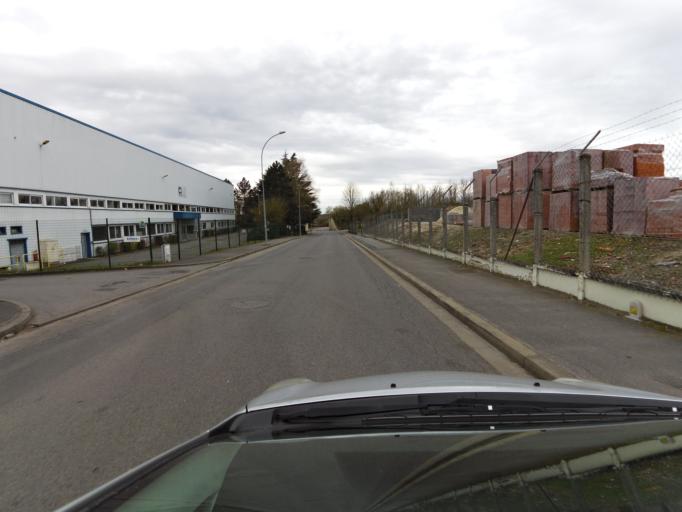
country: FR
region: Picardie
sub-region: Departement de l'Oise
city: Senlis
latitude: 49.2037
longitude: 2.5997
